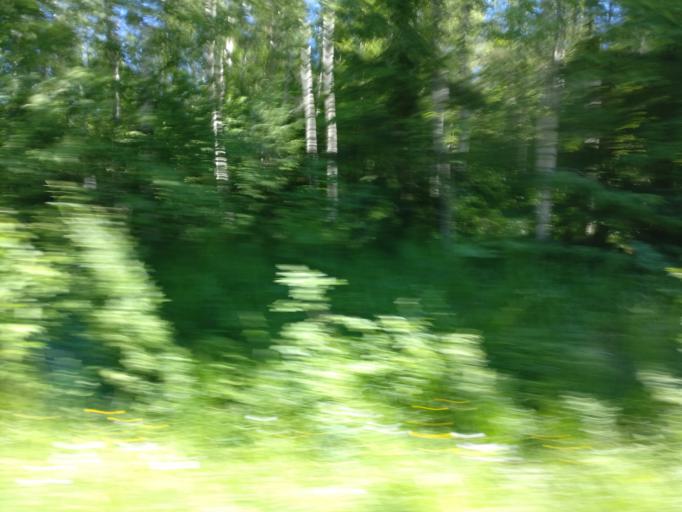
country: FI
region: Southern Savonia
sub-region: Savonlinna
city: Rantasalmi
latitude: 62.1126
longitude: 28.2595
